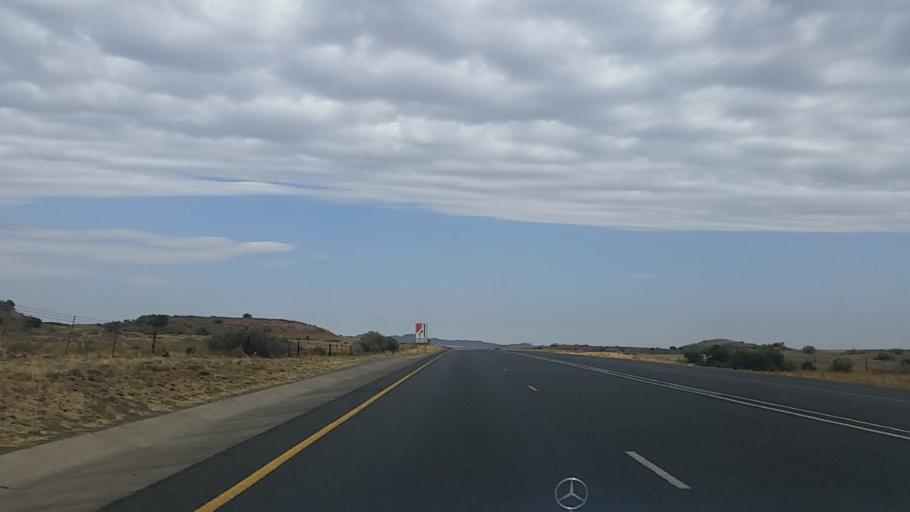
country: ZA
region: Northern Cape
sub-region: Pixley ka Seme District Municipality
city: Colesberg
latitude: -30.6194
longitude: 25.3286
